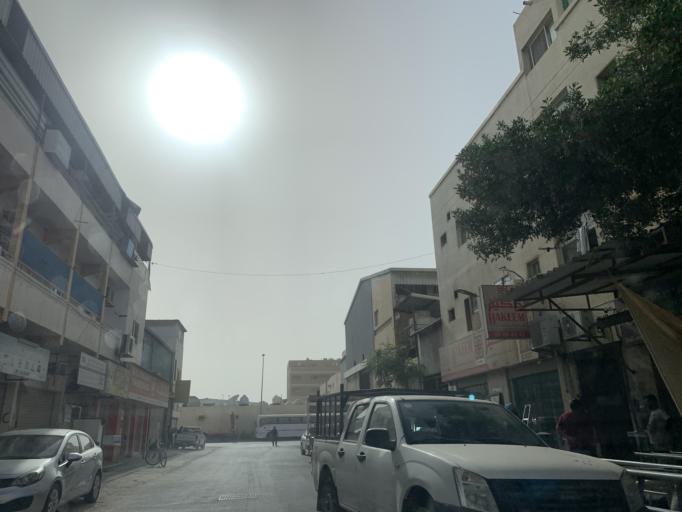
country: BH
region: Northern
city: Madinat `Isa
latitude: 26.1776
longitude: 50.5275
